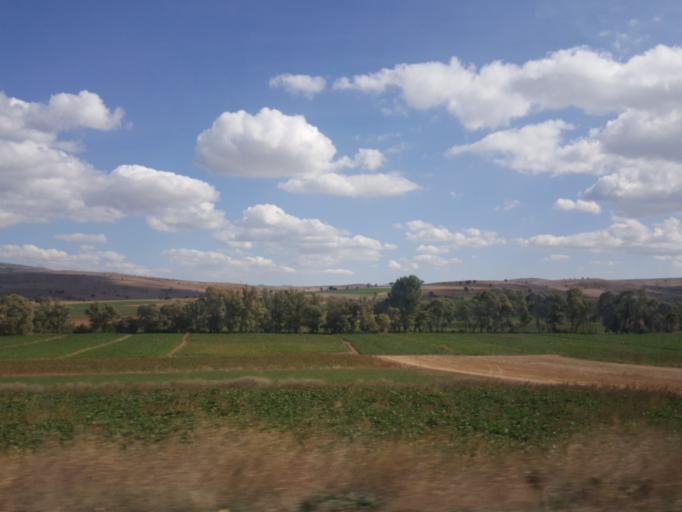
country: TR
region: Tokat
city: Camlibel
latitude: 40.1791
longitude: 36.4463
